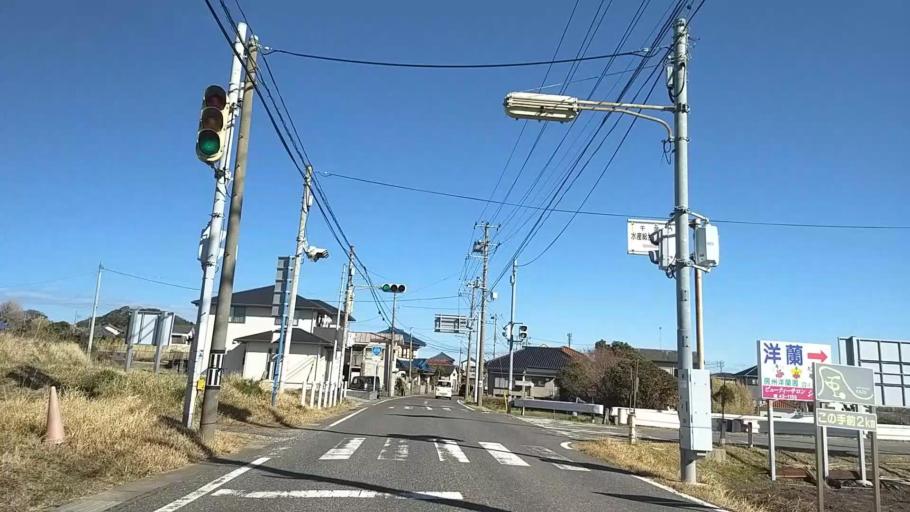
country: JP
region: Chiba
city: Tateyama
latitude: 34.9410
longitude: 139.9568
